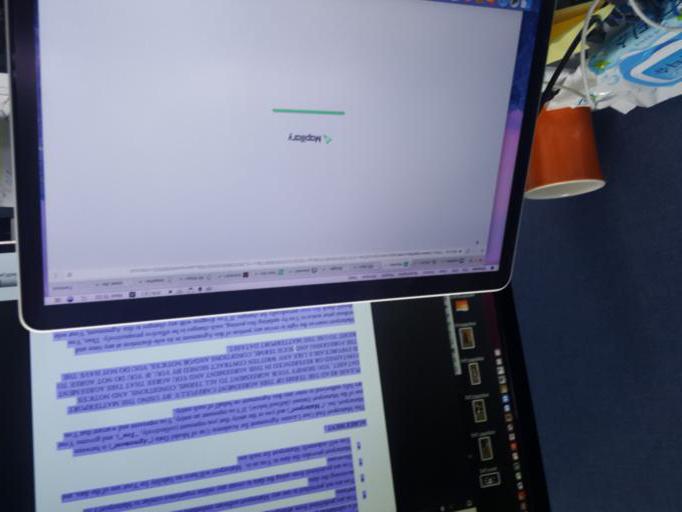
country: KR
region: Seoul
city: Seoul
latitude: 37.5790
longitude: 126.8909
